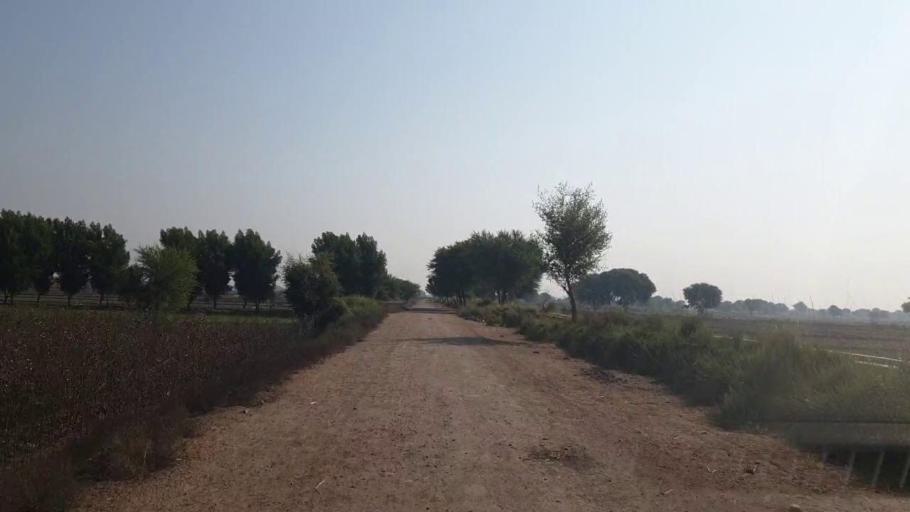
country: PK
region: Sindh
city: Sehwan
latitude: 26.4438
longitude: 67.8351
